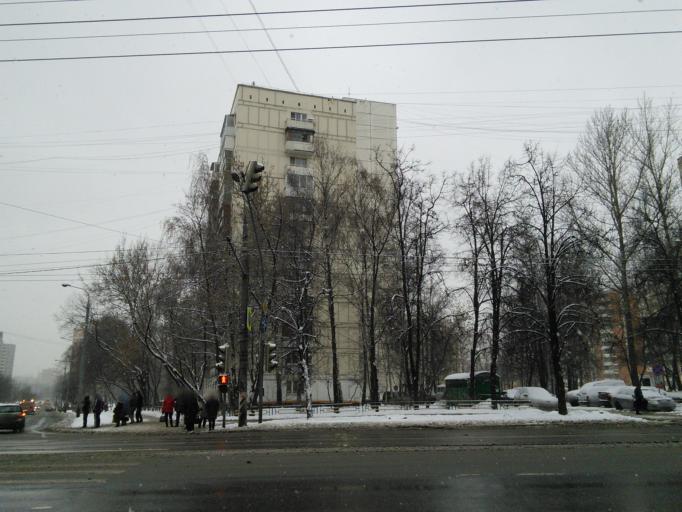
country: RU
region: Moscow
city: Vatutino
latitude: 55.8879
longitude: 37.6547
